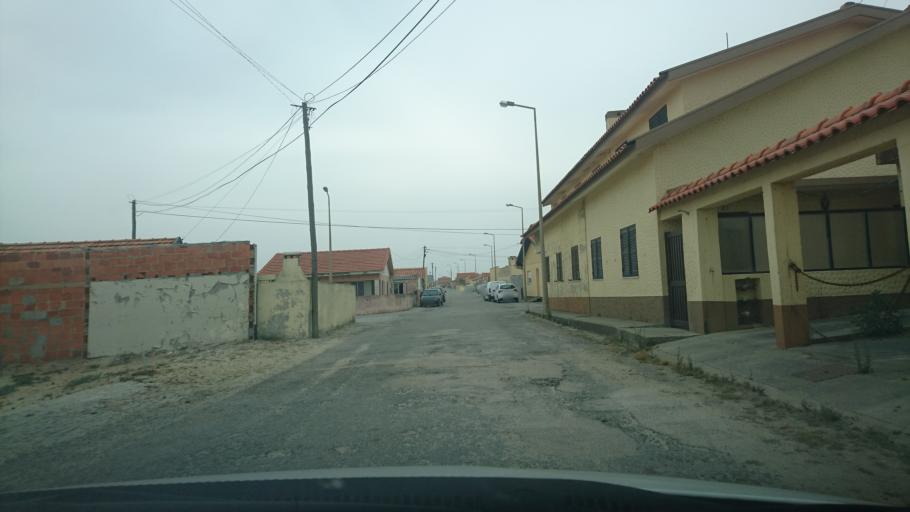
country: PT
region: Aveiro
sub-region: Ovar
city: Esmoriz
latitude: 40.9494
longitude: -8.6561
